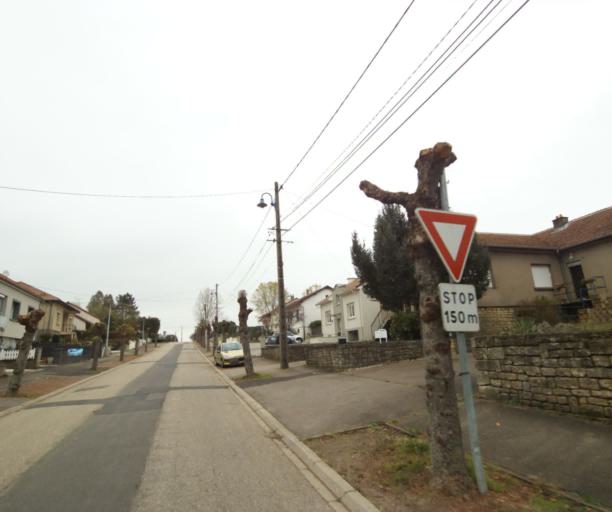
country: FR
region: Lorraine
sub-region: Departement de Meurthe-et-Moselle
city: Briey
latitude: 49.2698
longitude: 5.9177
